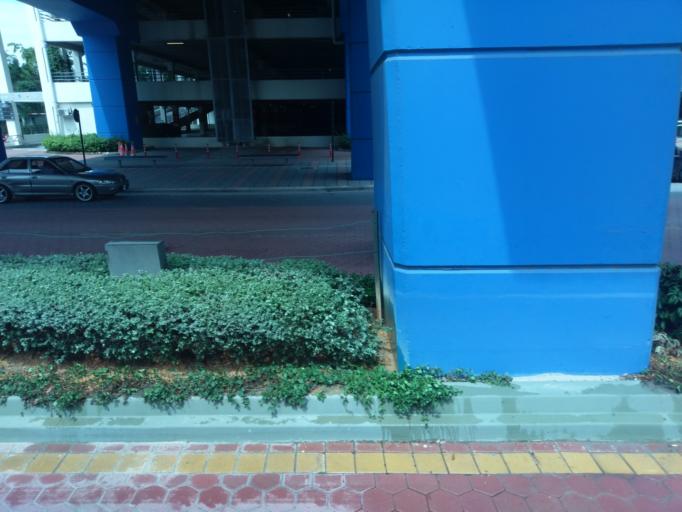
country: MY
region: Selangor
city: Subang Jaya
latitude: 3.0653
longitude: 101.6008
